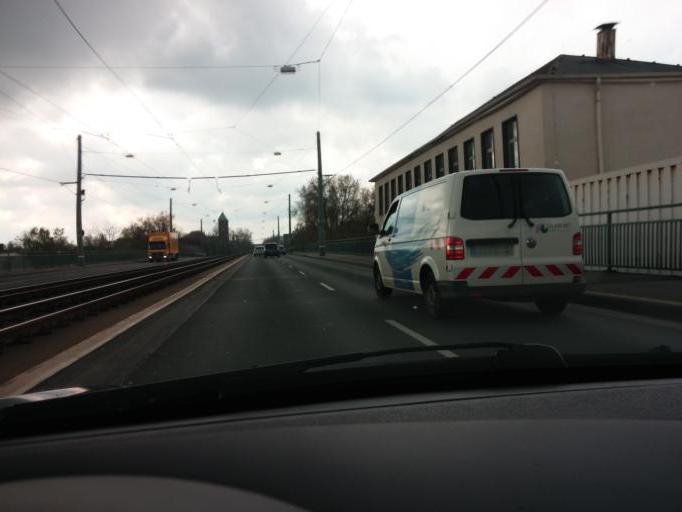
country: DE
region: North Rhine-Westphalia
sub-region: Regierungsbezirk Munster
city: Gelsenkirchen
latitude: 51.5245
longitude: 7.0881
